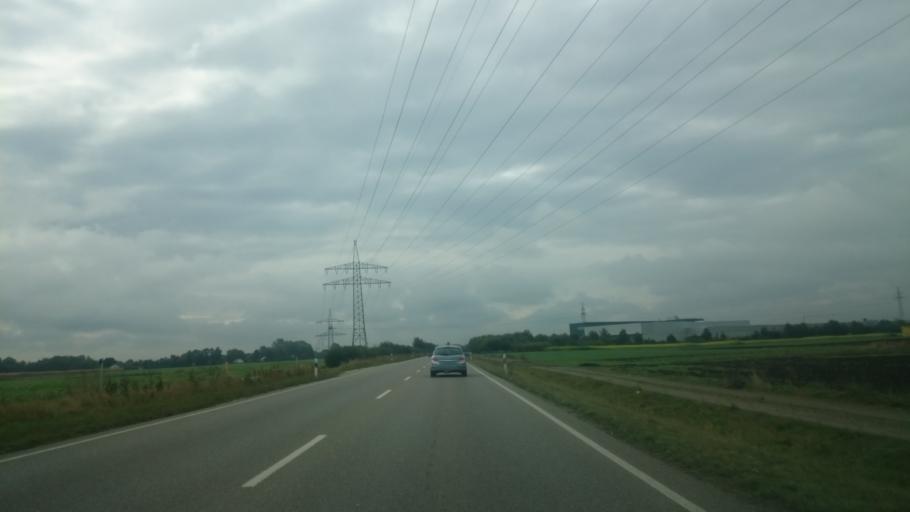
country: DE
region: Bavaria
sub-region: Swabia
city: Friedberg
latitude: 48.3717
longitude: 10.9603
